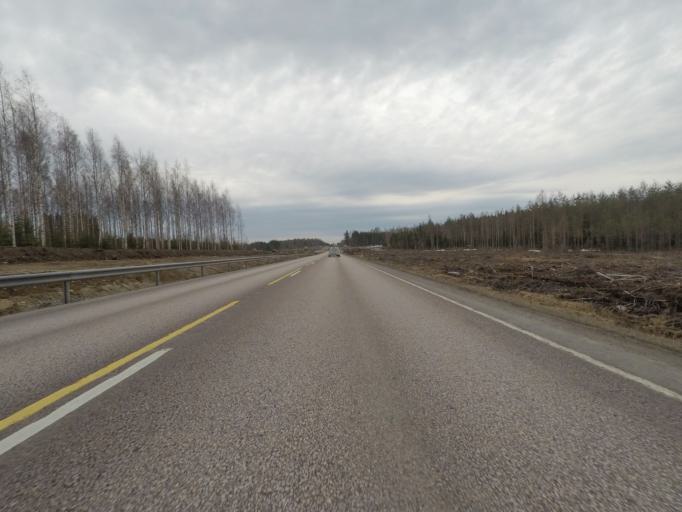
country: FI
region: Central Finland
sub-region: Joutsa
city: Leivonmaeki
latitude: 61.8633
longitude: 26.1032
